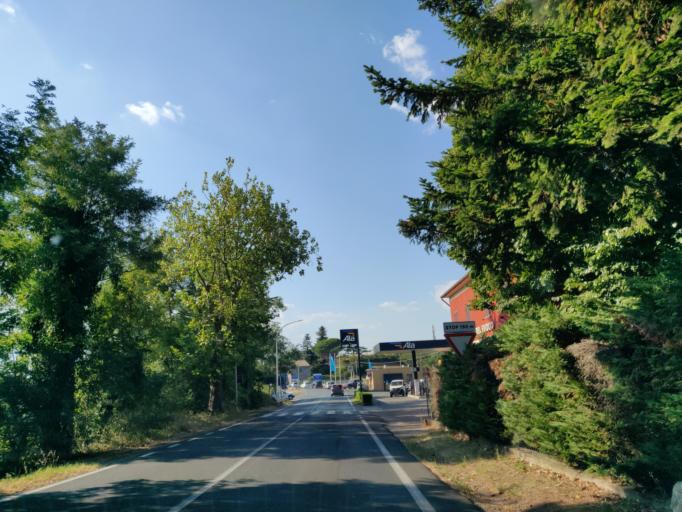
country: IT
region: Latium
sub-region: Provincia di Viterbo
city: Latera
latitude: 42.6315
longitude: 11.8351
